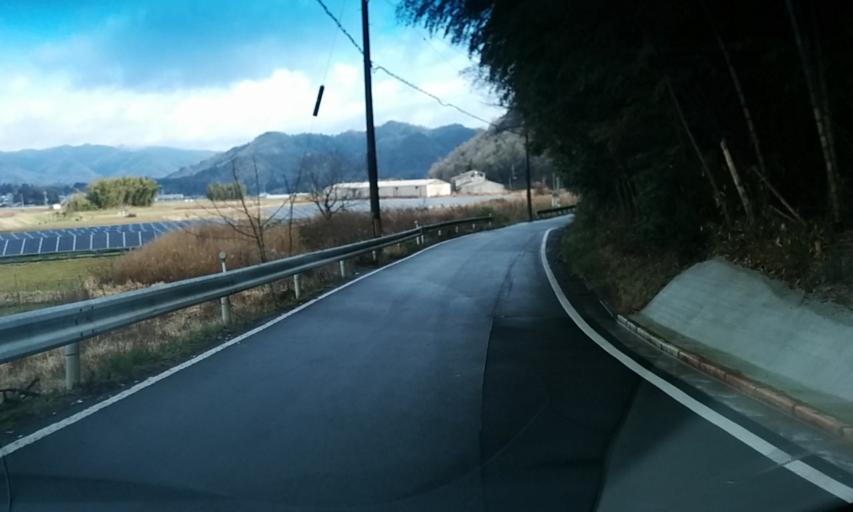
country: JP
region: Kyoto
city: Ayabe
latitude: 35.1783
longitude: 135.4100
